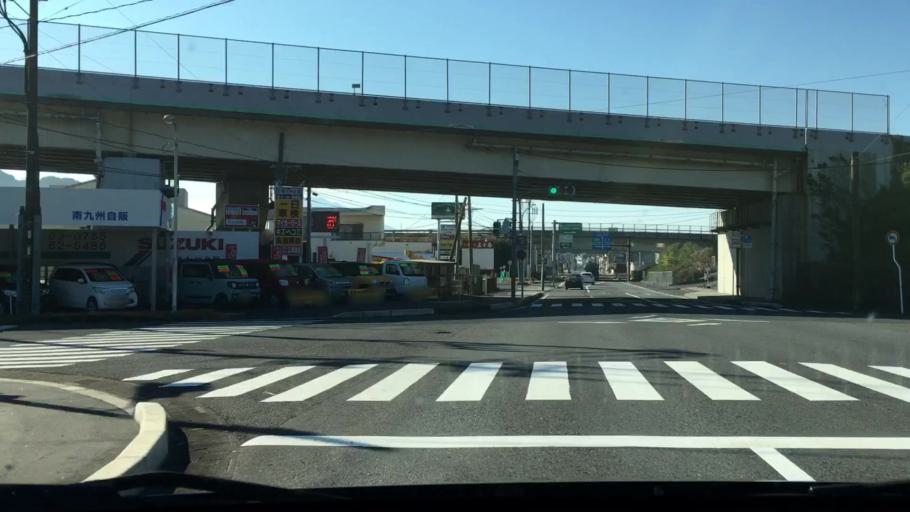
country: JP
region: Kagoshima
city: Kajiki
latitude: 31.7476
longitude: 130.6709
